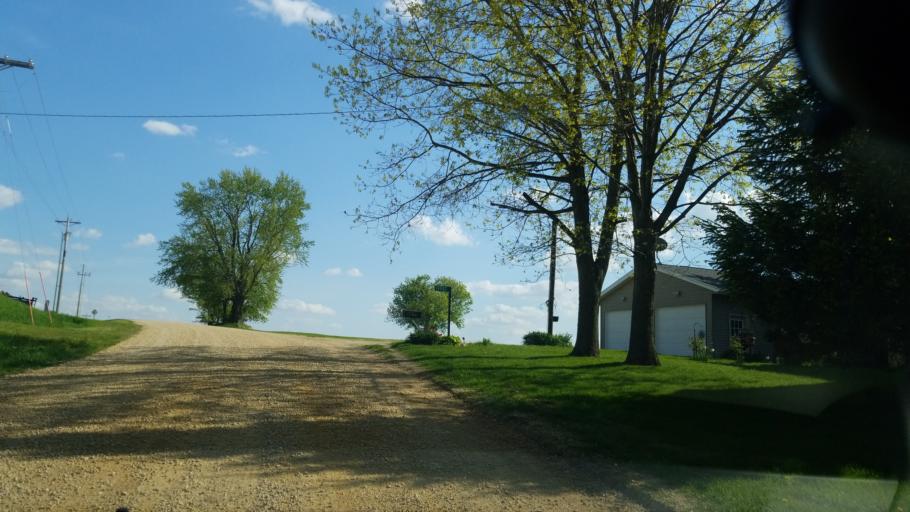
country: US
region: Iowa
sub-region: Jackson County
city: Maquoketa
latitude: 42.2074
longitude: -90.7301
